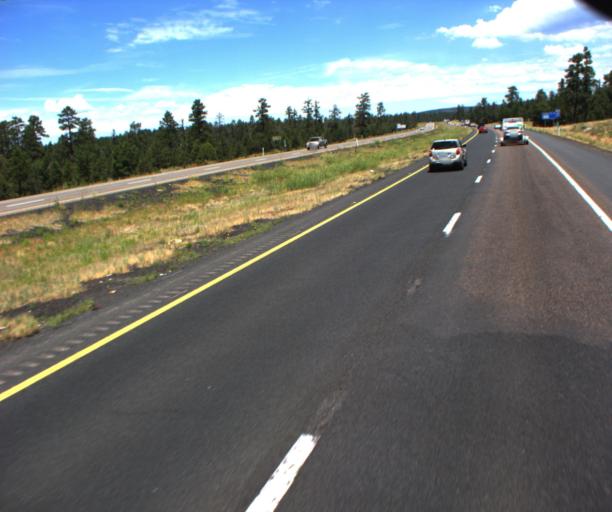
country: US
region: Arizona
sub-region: Coconino County
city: Sedona
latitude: 34.9184
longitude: -111.6423
